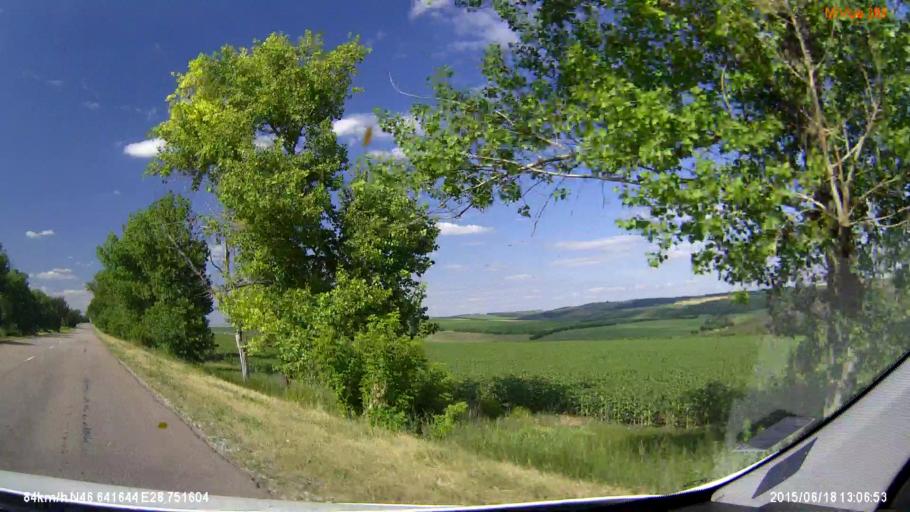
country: MD
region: Cimislia
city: Cimislia
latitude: 46.6414
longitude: 28.7516
